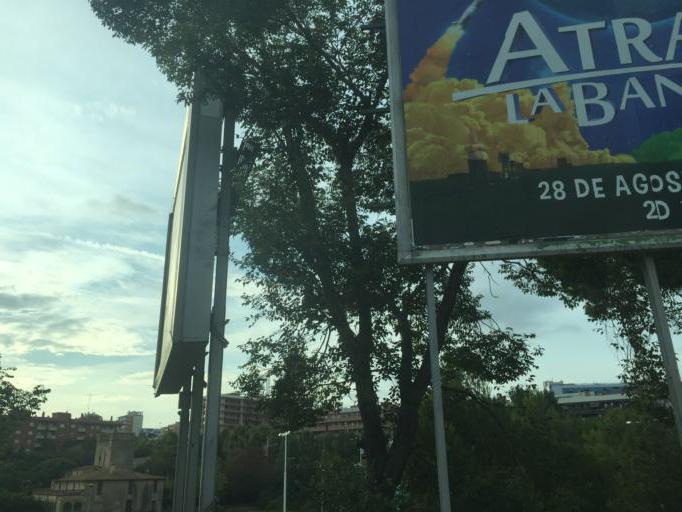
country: ES
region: Catalonia
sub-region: Provincia de Barcelona
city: Esplugues de Llobregat
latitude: 41.3758
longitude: 2.0960
